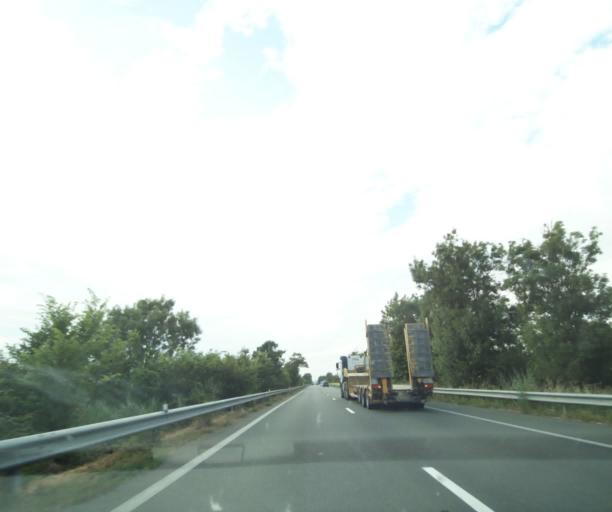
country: FR
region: Poitou-Charentes
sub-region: Departement de la Charente-Maritime
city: Chatelaillon-Plage
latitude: 46.0743
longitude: -1.0713
